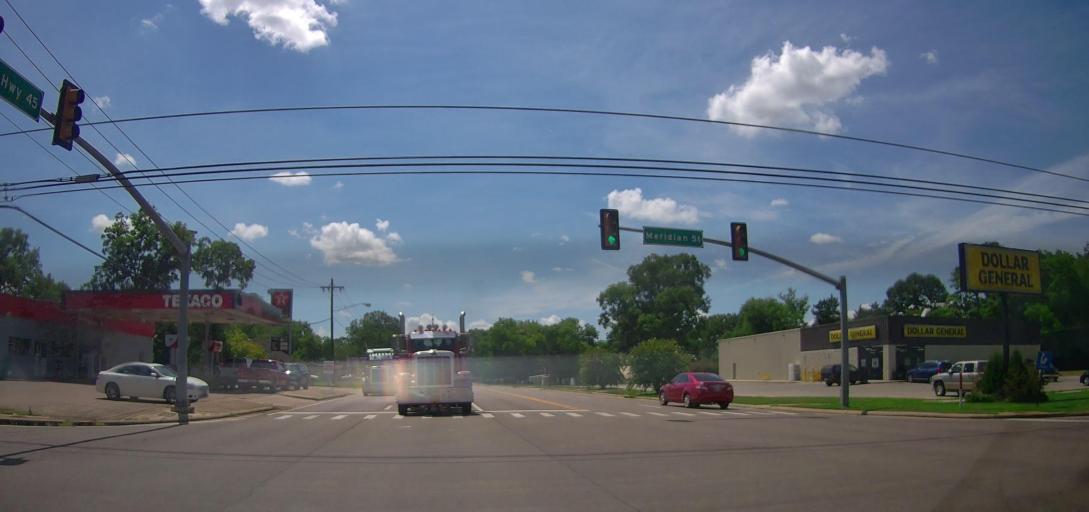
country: US
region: Mississippi
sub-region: Monroe County
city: Aberdeen
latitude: 33.8153
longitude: -88.5437
